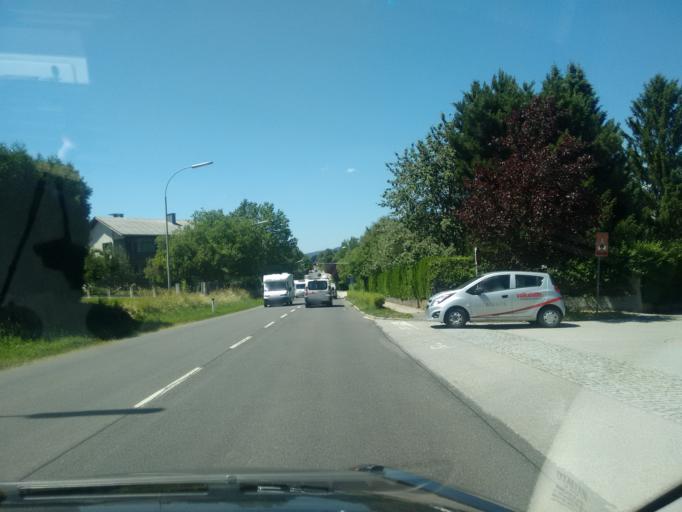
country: AT
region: Lower Austria
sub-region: Politischer Bezirk Sankt Polten
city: Gerersdorf
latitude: 48.2001
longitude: 15.5584
